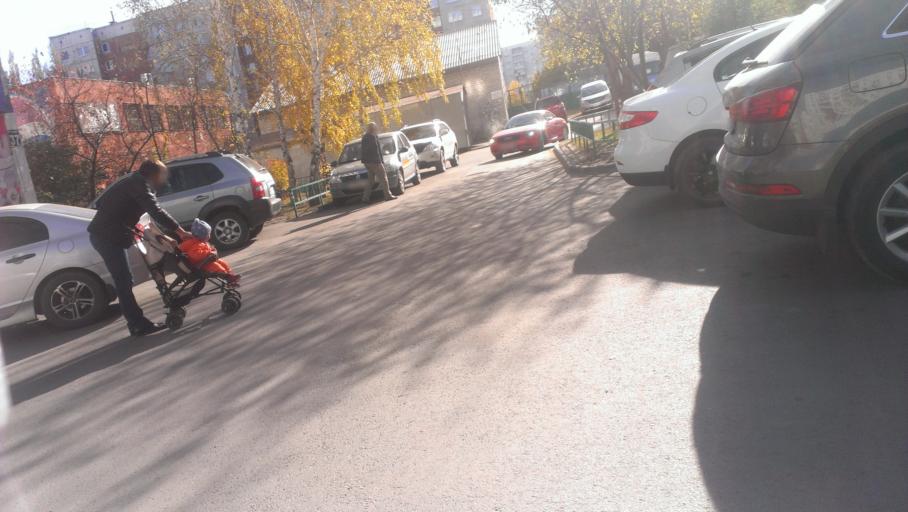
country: RU
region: Altai Krai
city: Novosilikatnyy
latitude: 53.3339
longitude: 83.6780
